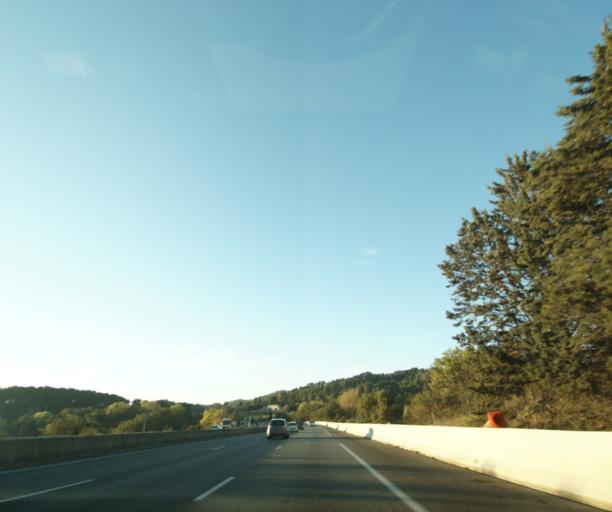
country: FR
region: Provence-Alpes-Cote d'Azur
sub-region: Departement des Bouches-du-Rhone
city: Le Tholonet
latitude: 43.5105
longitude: 5.4975
